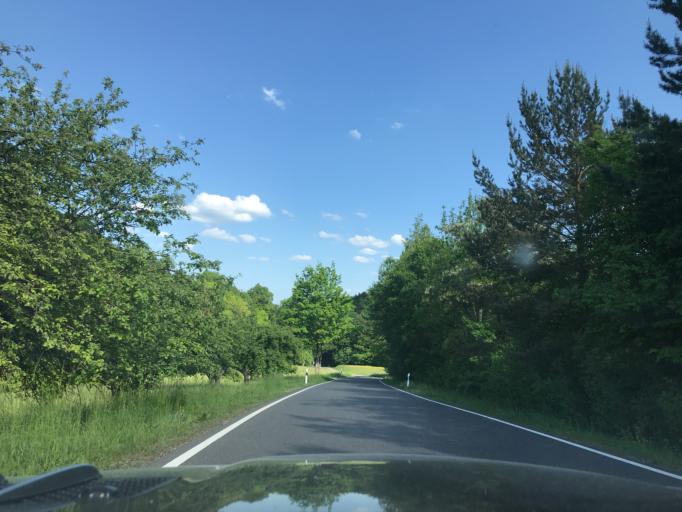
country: DE
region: Thuringia
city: Behringen
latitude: 50.7845
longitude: 10.9811
